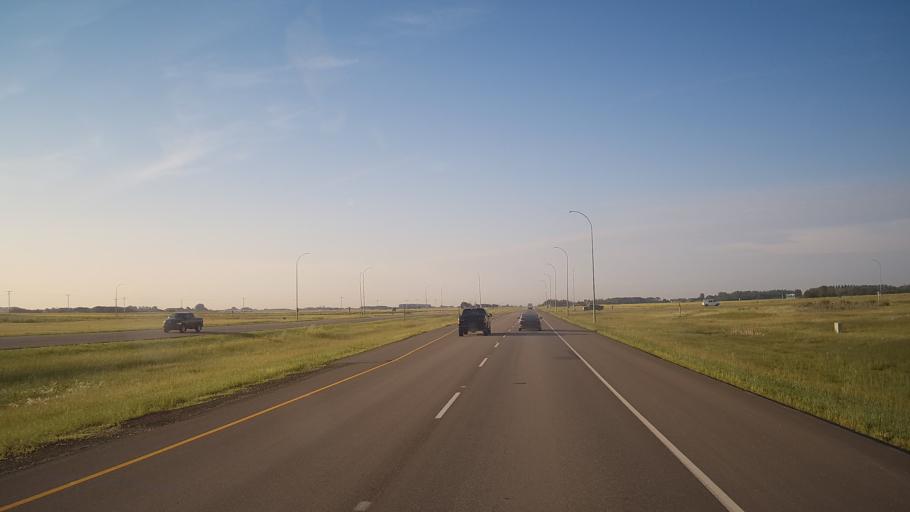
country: CA
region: Saskatchewan
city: Saskatoon
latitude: 52.0560
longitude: -106.5990
